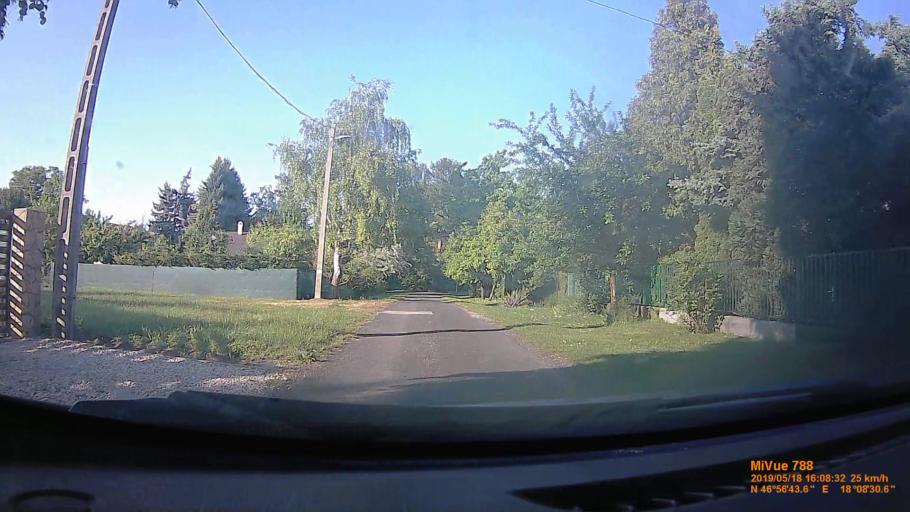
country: HU
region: Somogy
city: Balatonszabadi
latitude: 46.9455
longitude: 18.1419
